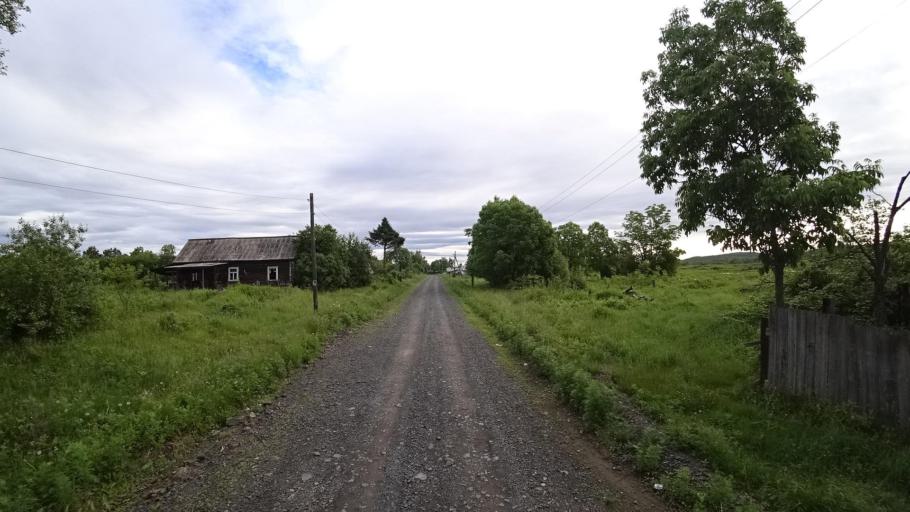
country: RU
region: Khabarovsk Krai
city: Amursk
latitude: 49.8884
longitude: 136.1289
